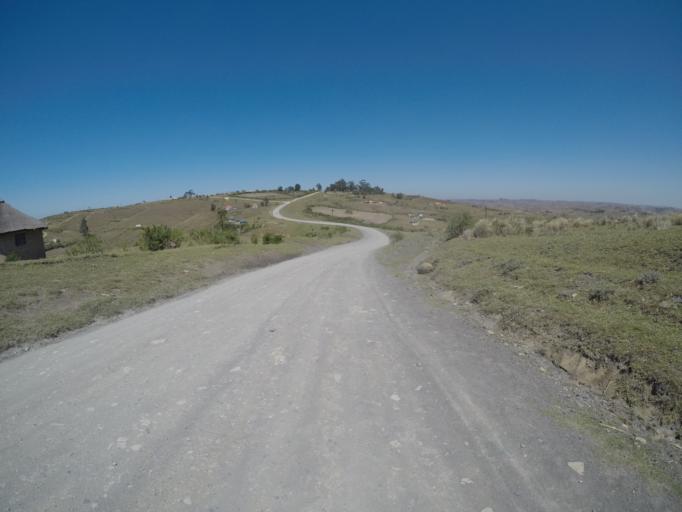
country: ZA
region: Eastern Cape
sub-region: OR Tambo District Municipality
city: Libode
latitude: -31.9774
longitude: 29.0356
